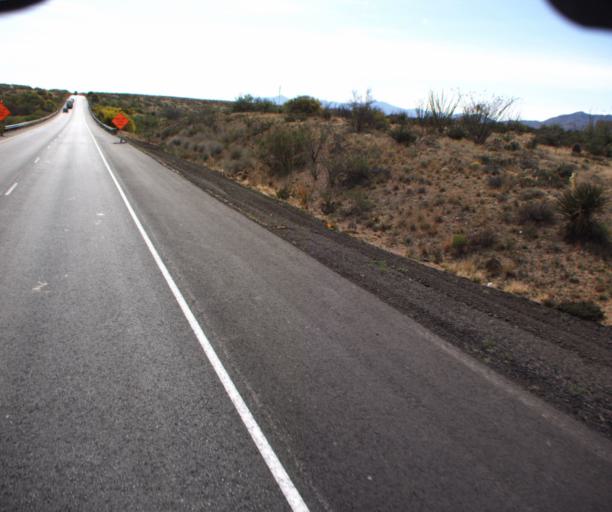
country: US
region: Arizona
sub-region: Pima County
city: Vail
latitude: 31.9998
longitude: -110.6731
